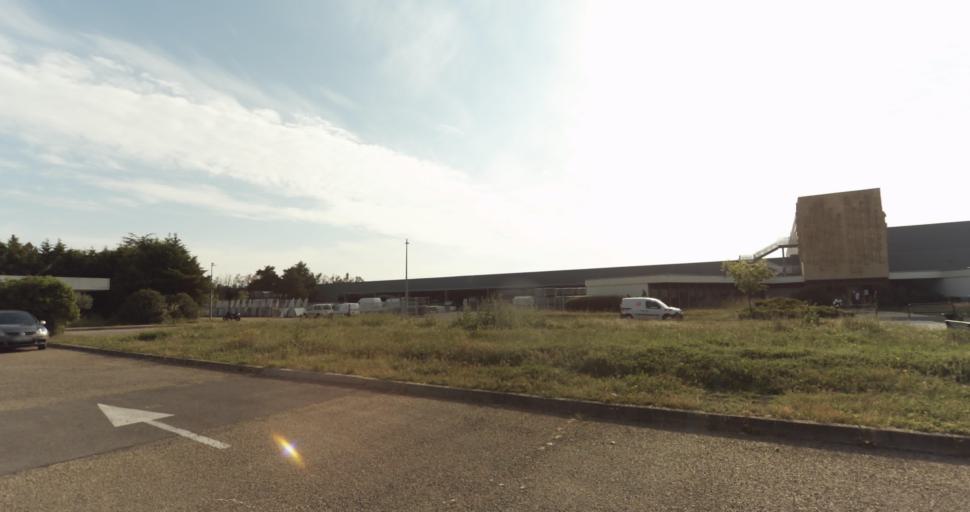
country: FR
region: Languedoc-Roussillon
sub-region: Departement du Gard
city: Rodilhan
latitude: 43.8361
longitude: 4.4103
